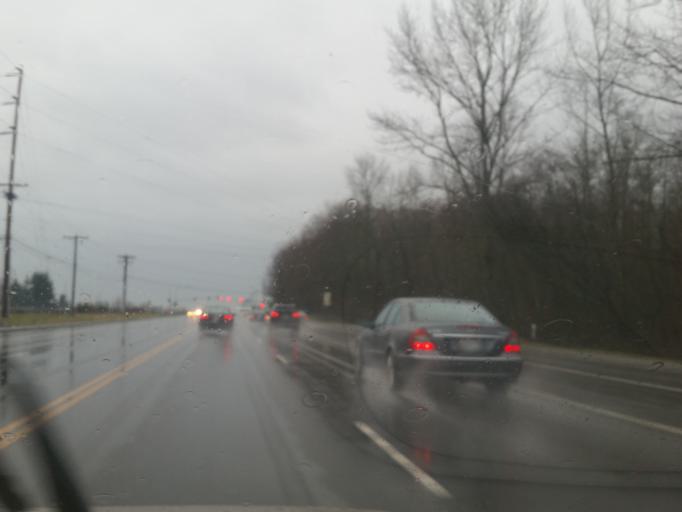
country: US
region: Washington
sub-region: Snohomish County
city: Mukilteo
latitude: 47.9161
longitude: -122.2717
